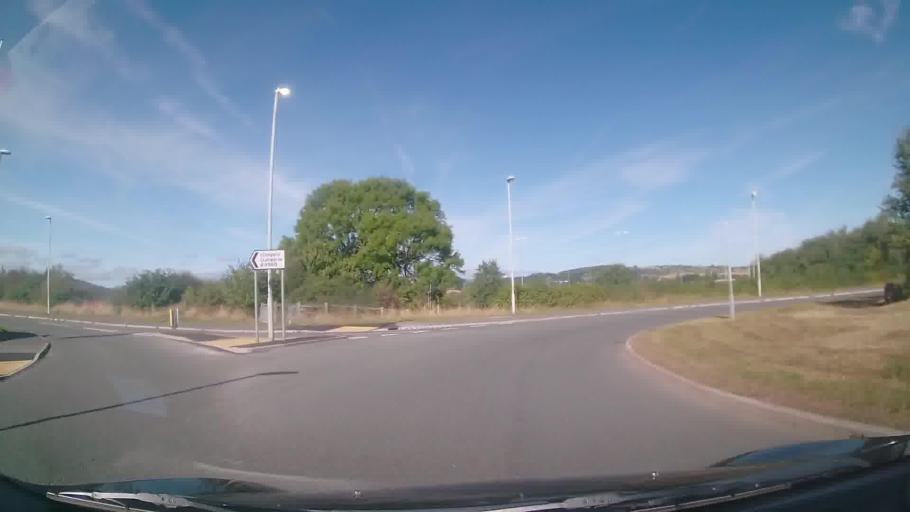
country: GB
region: Wales
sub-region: Sir Powys
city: Hay
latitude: 51.9944
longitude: -3.2367
